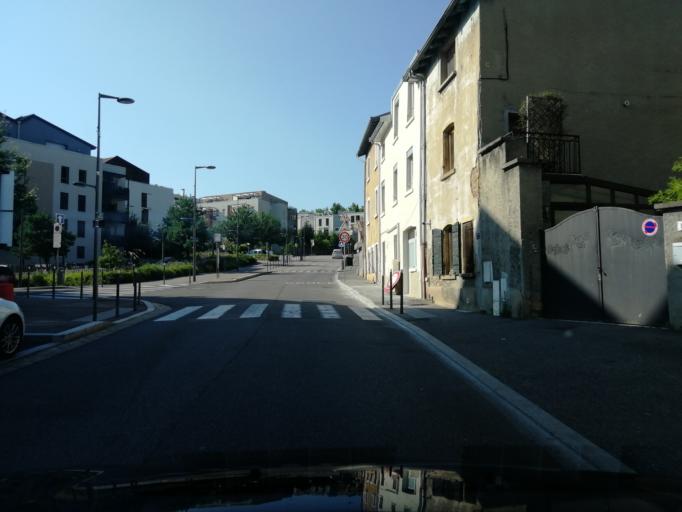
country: FR
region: Rhone-Alpes
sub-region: Departement du Rhone
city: Fontaines-sur-Saone
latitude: 45.8358
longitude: 4.8472
